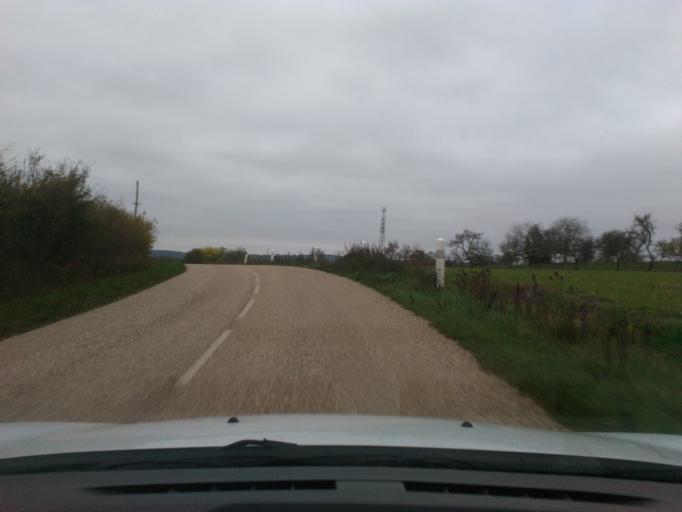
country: FR
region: Lorraine
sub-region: Departement des Vosges
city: Dogneville
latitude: 48.2792
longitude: 6.4824
